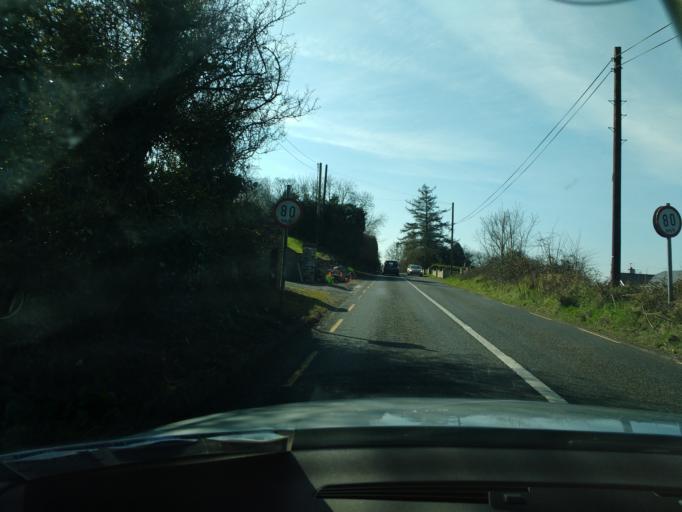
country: IE
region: Munster
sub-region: County Limerick
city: Castleconnell
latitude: 52.6875
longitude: -8.4833
